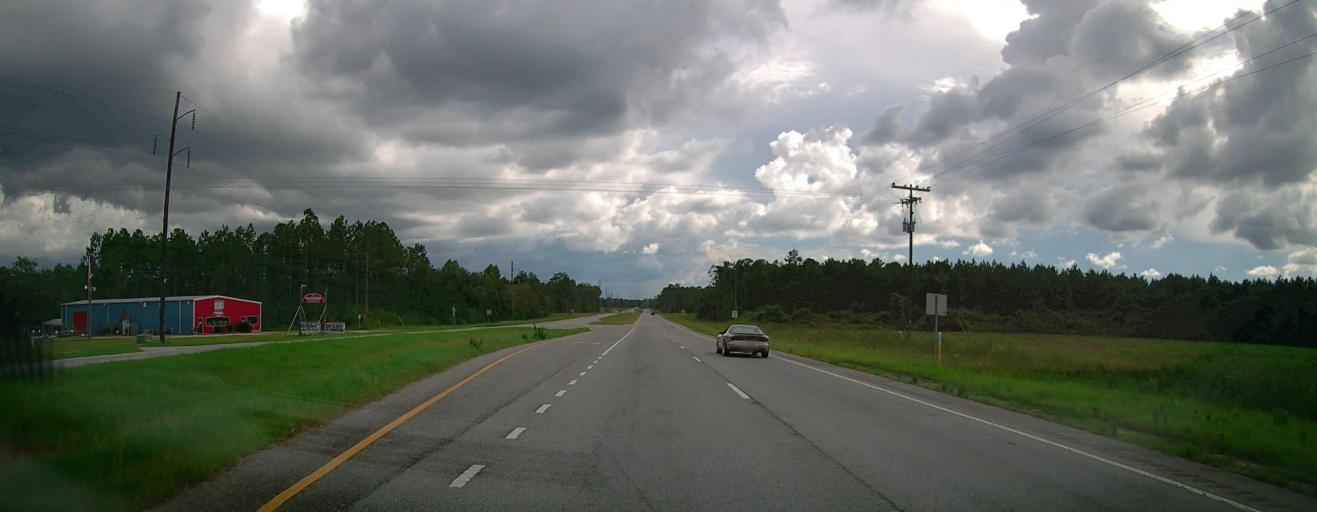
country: US
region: Georgia
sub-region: Pierce County
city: Blackshear
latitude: 31.4252
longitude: -82.0963
